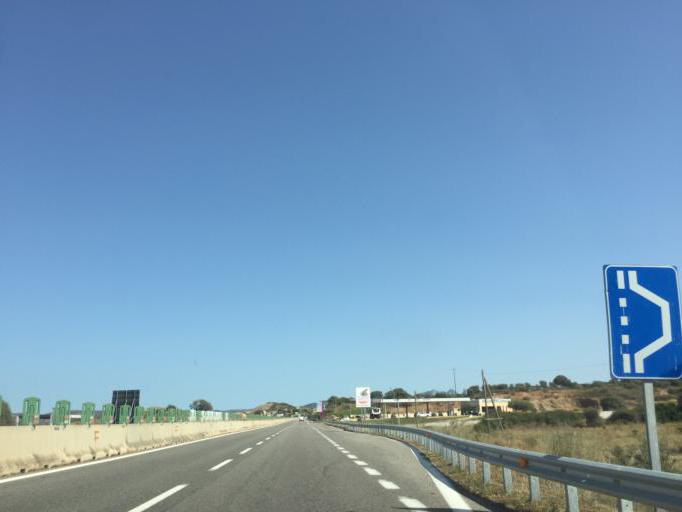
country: IT
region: Sardinia
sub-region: Provincia di Olbia-Tempio
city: Olbia
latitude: 40.8886
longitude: 9.4917
